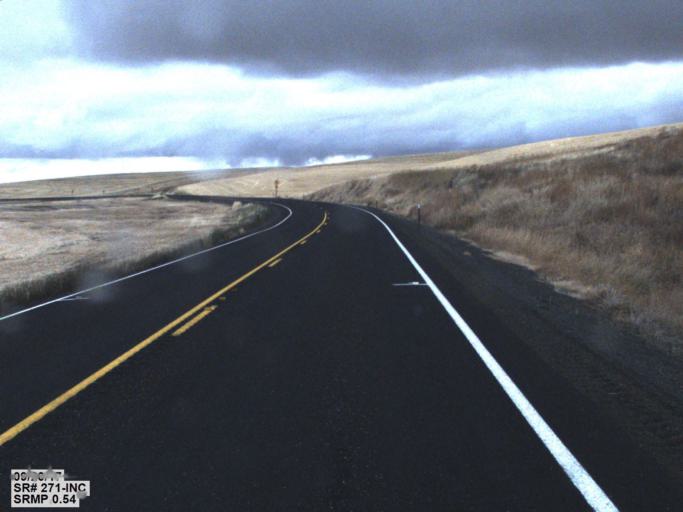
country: US
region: Washington
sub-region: Whitman County
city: Colfax
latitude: 47.1418
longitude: -117.2489
